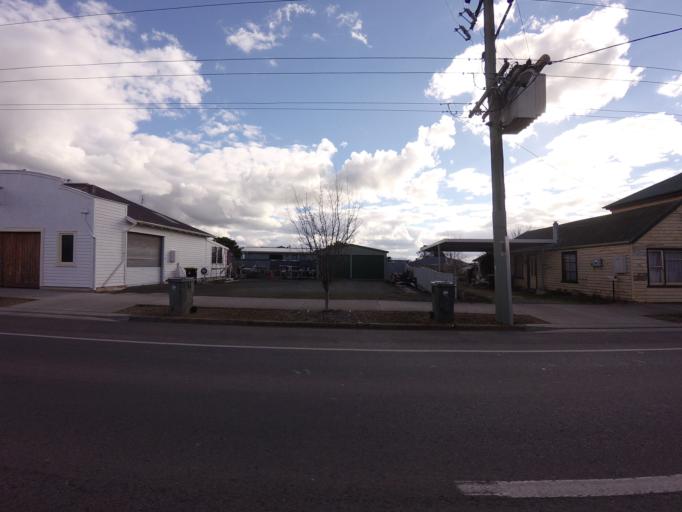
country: AU
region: Tasmania
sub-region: Northern Midlands
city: Longford
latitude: -41.6844
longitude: 147.0806
